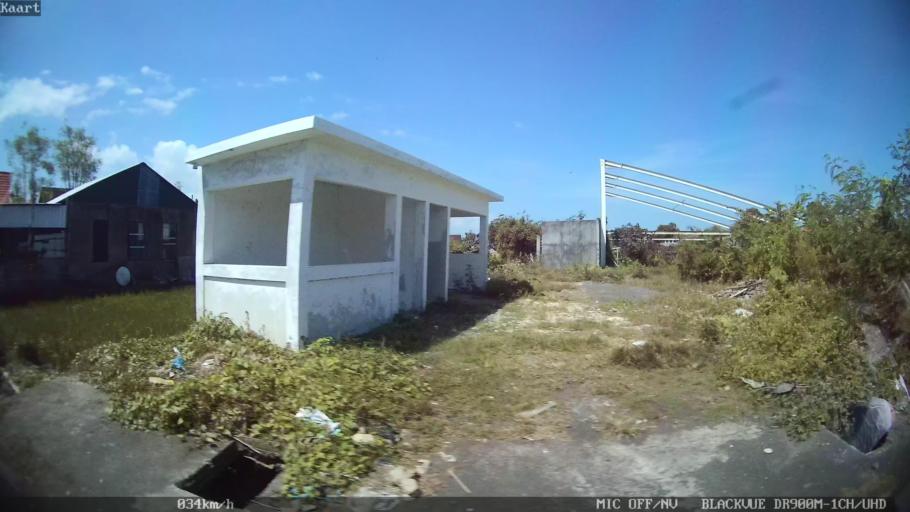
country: ID
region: Bali
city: Denpasar
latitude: -8.6637
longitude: 115.1683
